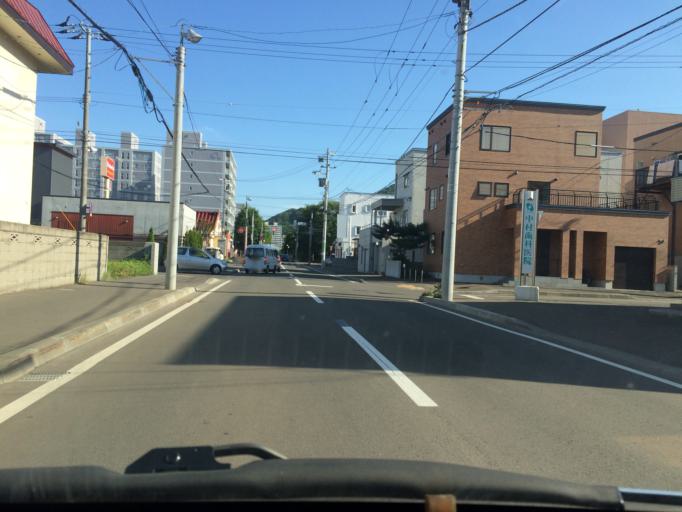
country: JP
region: Hokkaido
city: Sapporo
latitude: 43.0314
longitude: 141.3413
